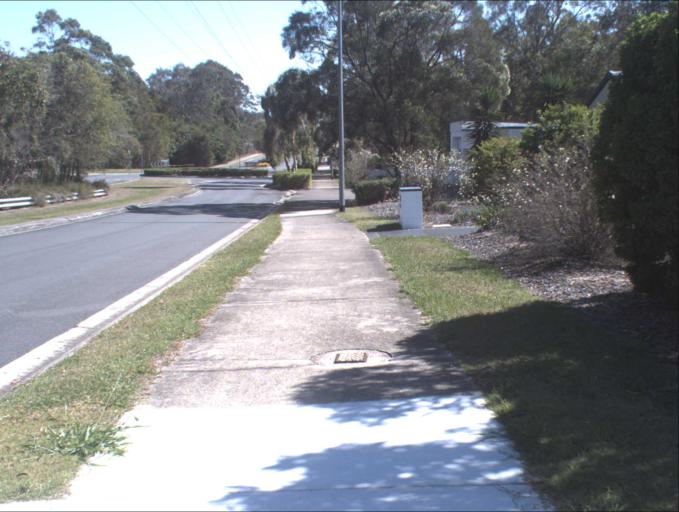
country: AU
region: Queensland
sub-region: Logan
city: Springwood
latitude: -27.6138
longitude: 153.1428
